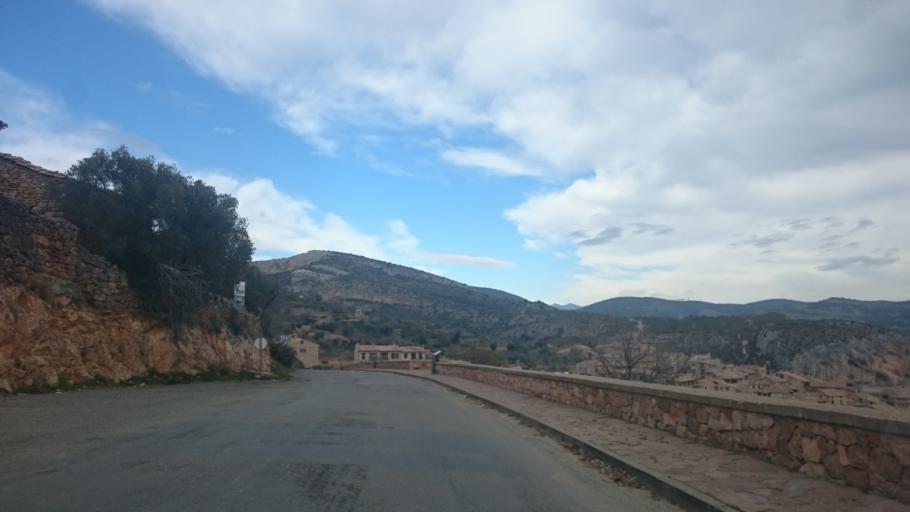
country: ES
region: Aragon
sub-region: Provincia de Huesca
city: Alquezar
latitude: 42.1701
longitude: 0.0228
